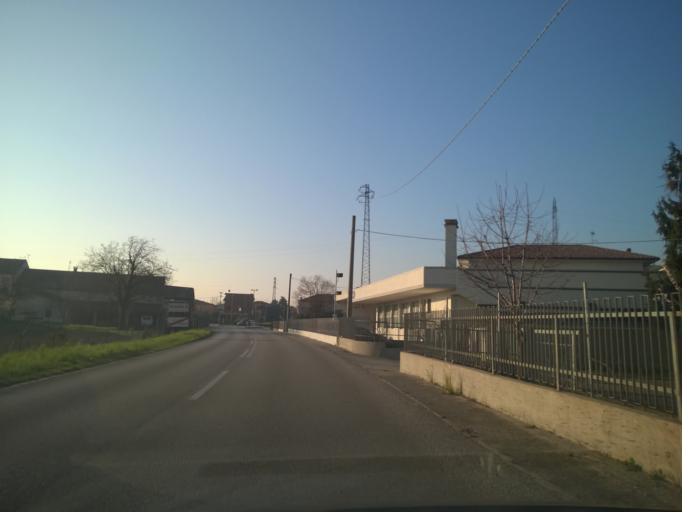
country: IT
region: Veneto
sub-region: Provincia di Vicenza
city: Villaggio Montegrappa
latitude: 45.5431
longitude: 11.6169
